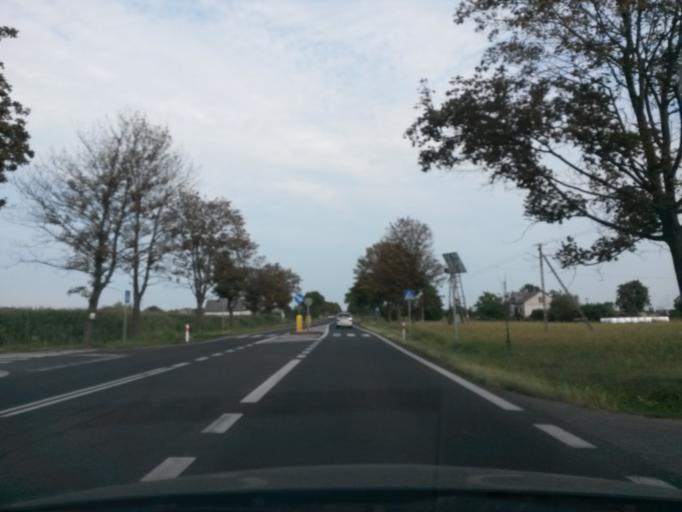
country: PL
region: Masovian Voivodeship
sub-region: Powiat sierpecki
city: Zawidz
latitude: 52.8147
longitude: 19.7962
